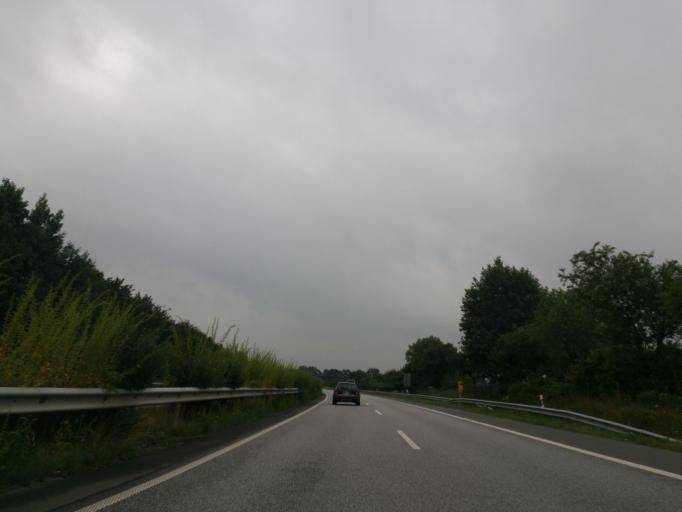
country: DE
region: Schleswig-Holstein
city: Schafstedt
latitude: 54.0848
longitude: 9.2676
